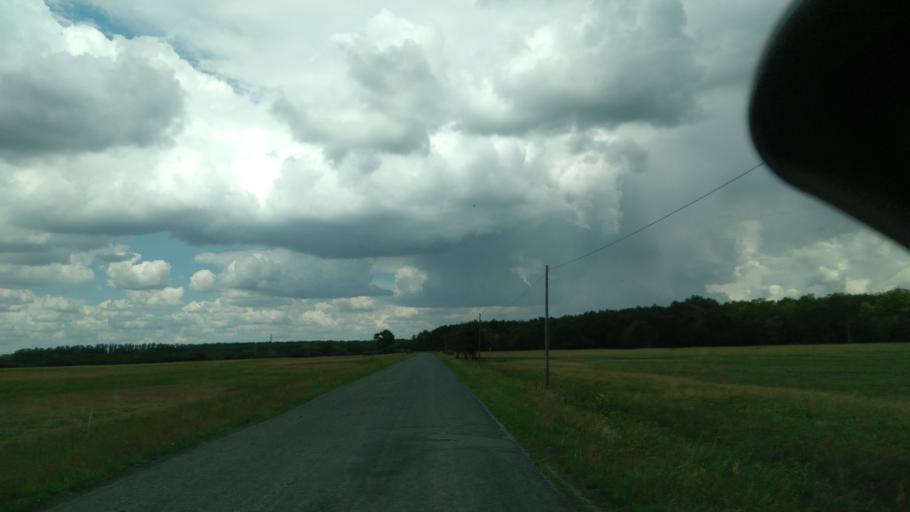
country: HU
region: Bekes
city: Szeghalom
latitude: 47.1061
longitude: 21.0836
